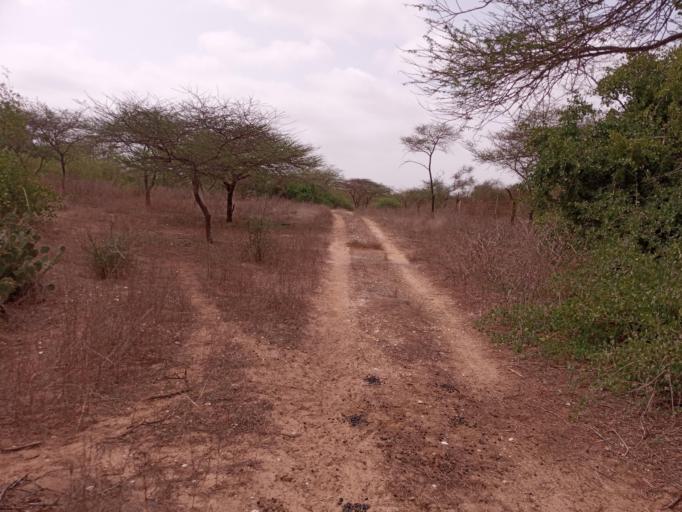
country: SN
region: Saint-Louis
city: Saint-Louis
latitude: 15.9244
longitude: -16.4537
